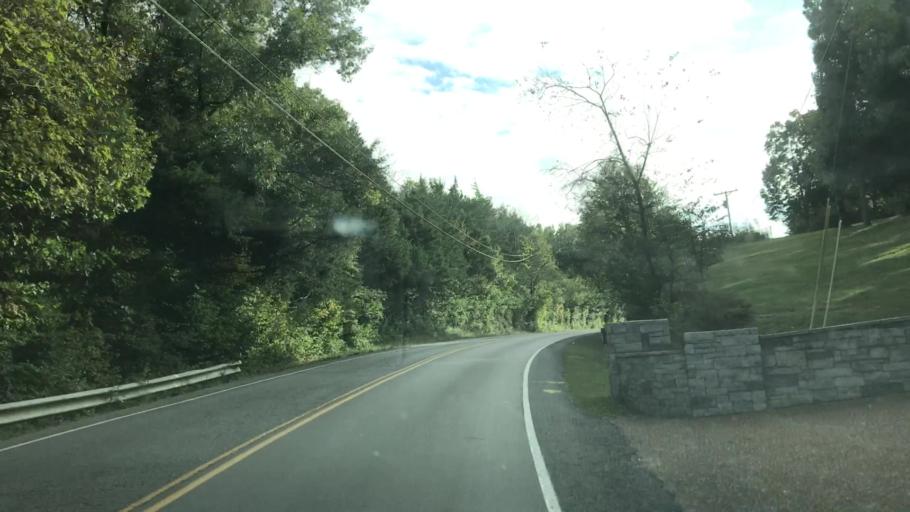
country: US
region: Tennessee
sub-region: Davidson County
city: Forest Hills
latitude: 36.0433
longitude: -86.9045
